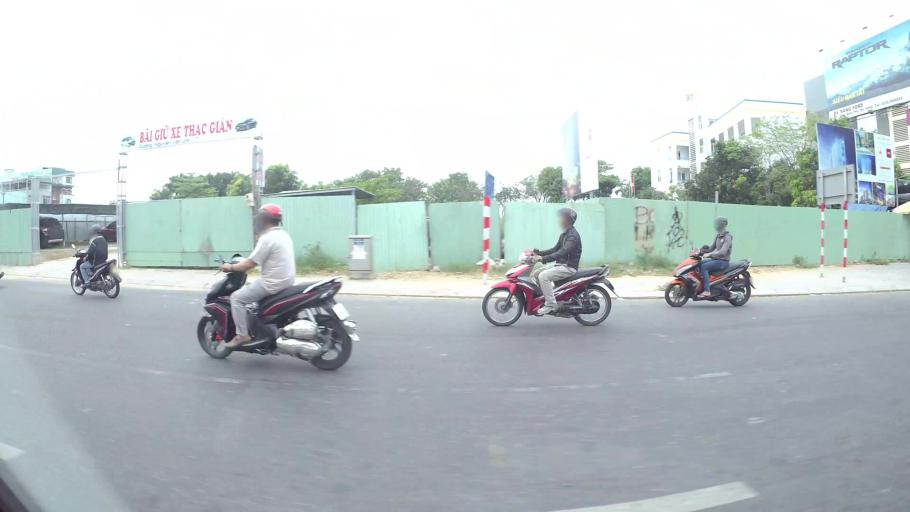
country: VN
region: Da Nang
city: Da Nang
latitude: 16.0592
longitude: 108.2066
